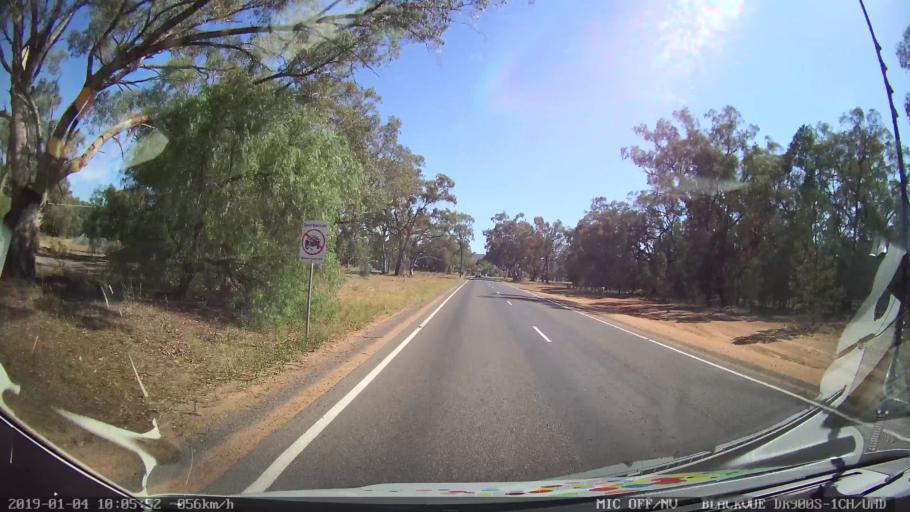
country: AU
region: New South Wales
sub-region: Cabonne
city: Canowindra
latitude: -33.4373
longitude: 148.3666
